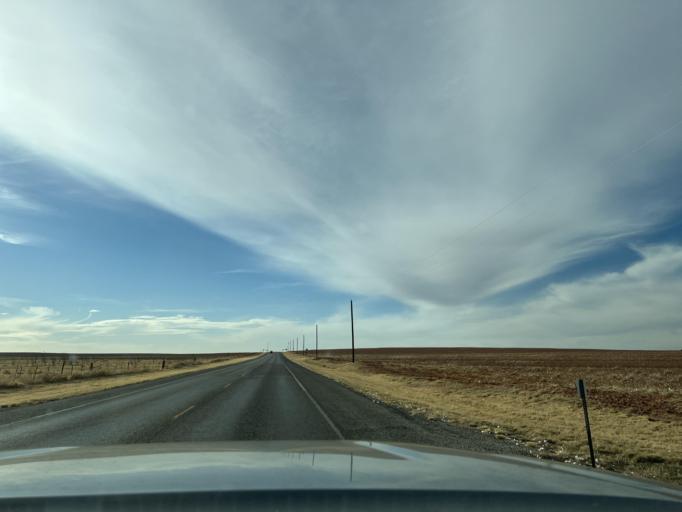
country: US
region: Texas
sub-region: Fisher County
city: Roby
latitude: 32.7408
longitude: -100.4843
